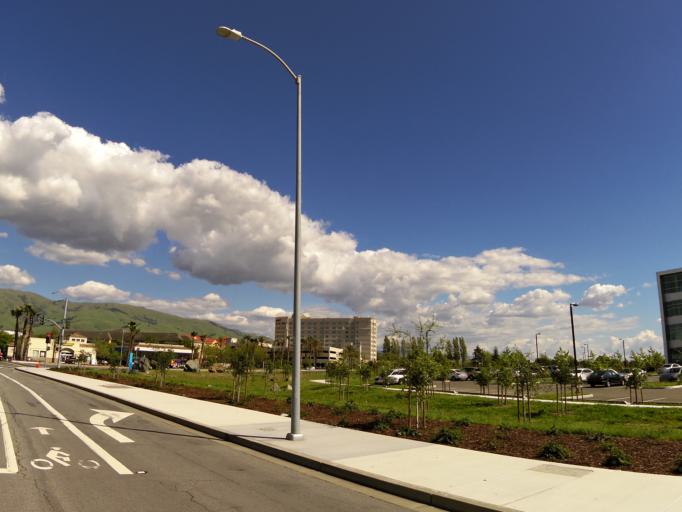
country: US
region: California
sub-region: Alameda County
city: Fremont
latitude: 37.4903
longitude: -121.9496
